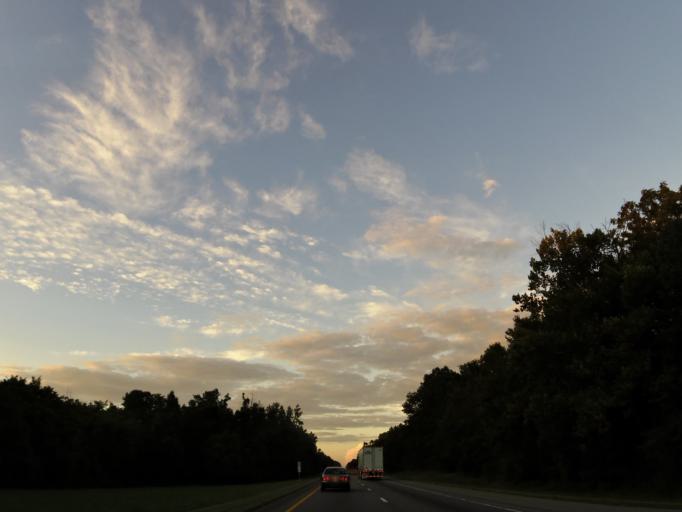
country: US
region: Tennessee
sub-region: Monroe County
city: Sweetwater
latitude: 35.5633
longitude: -84.5499
